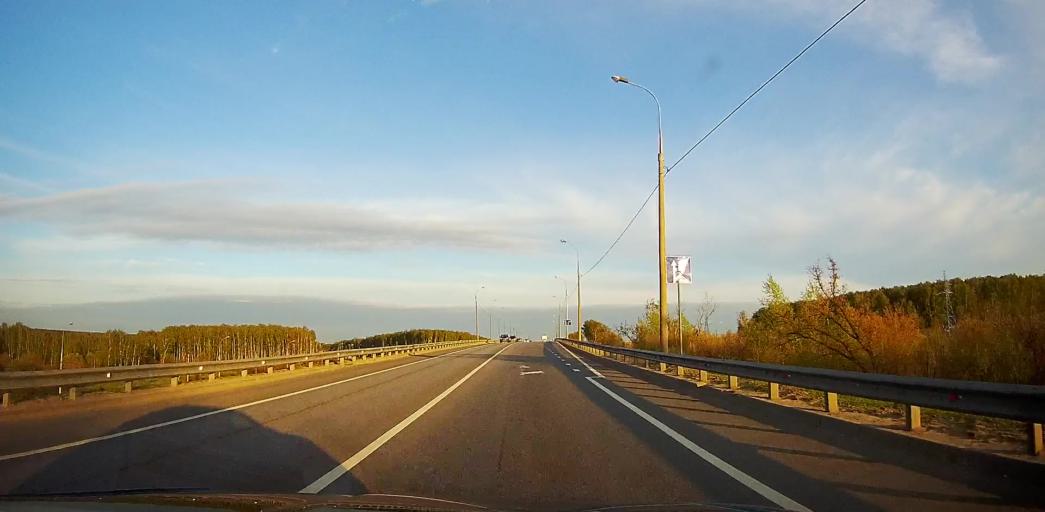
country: RU
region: Moskovskaya
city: Troitskoye
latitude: 55.2377
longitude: 38.5440
